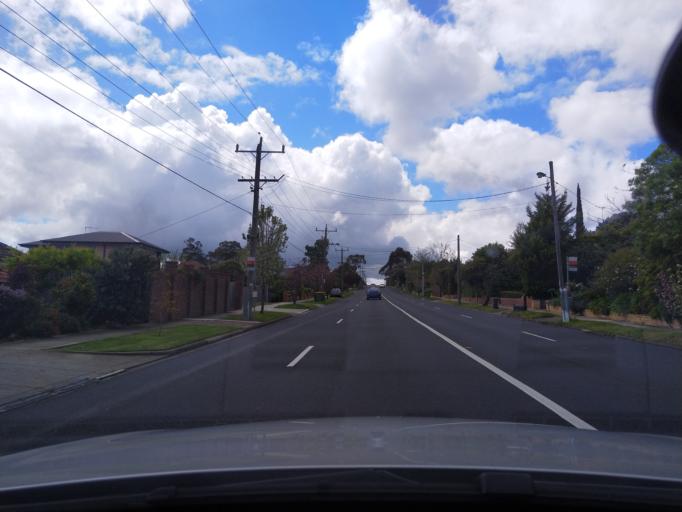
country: AU
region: Victoria
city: Macleod
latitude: -37.7406
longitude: 145.0690
